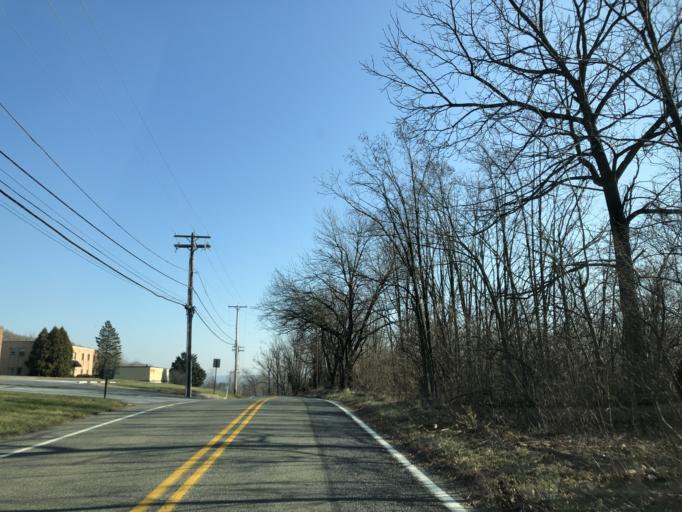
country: US
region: Pennsylvania
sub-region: Chester County
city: Malvern
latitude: 40.0733
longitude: -75.5280
